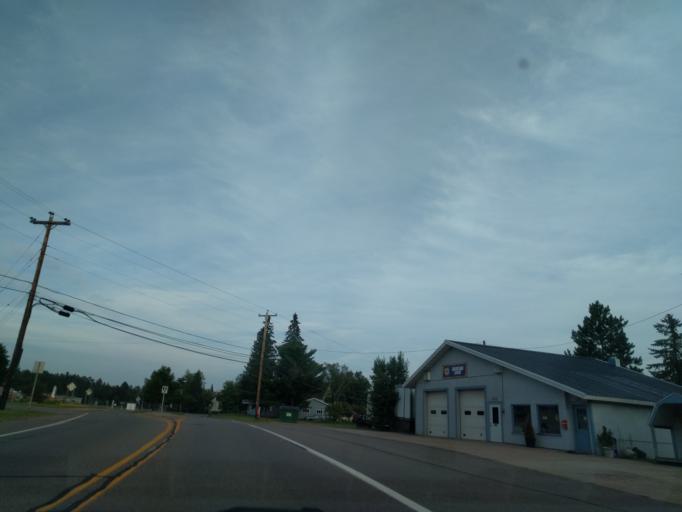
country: US
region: Michigan
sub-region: Marquette County
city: Gwinn
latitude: 46.2850
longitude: -87.4470
